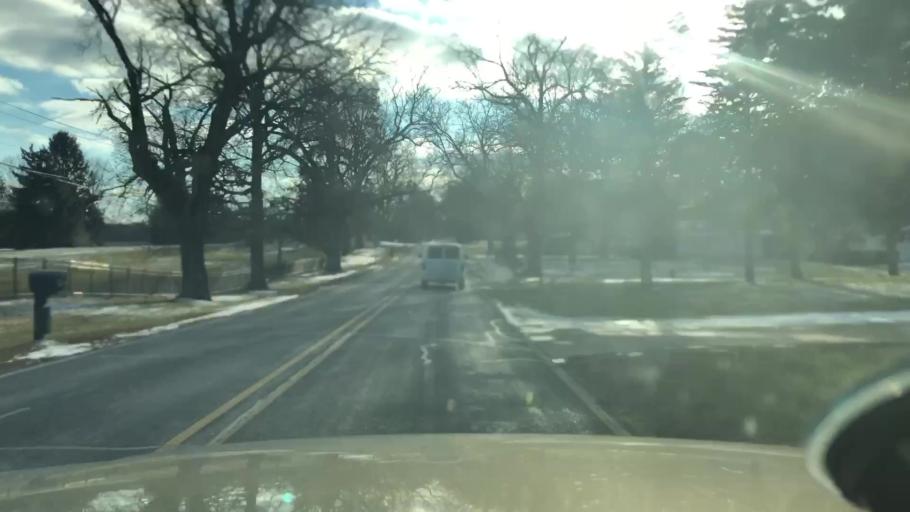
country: US
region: Michigan
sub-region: Jackson County
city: Vandercook Lake
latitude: 42.1919
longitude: -84.4520
